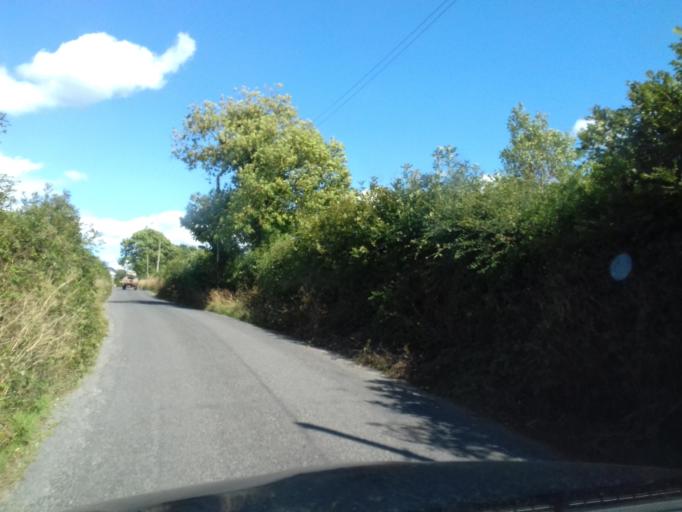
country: IE
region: Leinster
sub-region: Kilkenny
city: Callan
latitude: 52.5388
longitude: -7.3252
